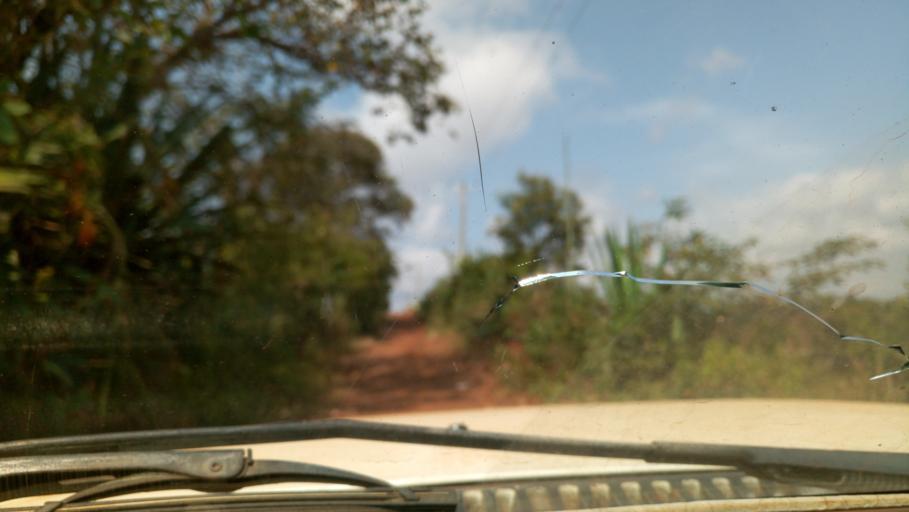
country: KE
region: Murang'a District
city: Maragua
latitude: -0.8780
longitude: 37.1280
